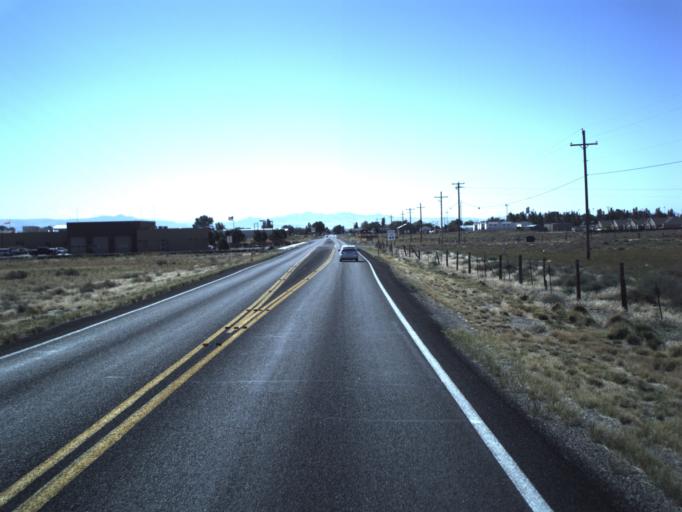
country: US
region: Utah
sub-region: Beaver County
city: Milford
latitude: 38.4097
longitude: -113.0099
